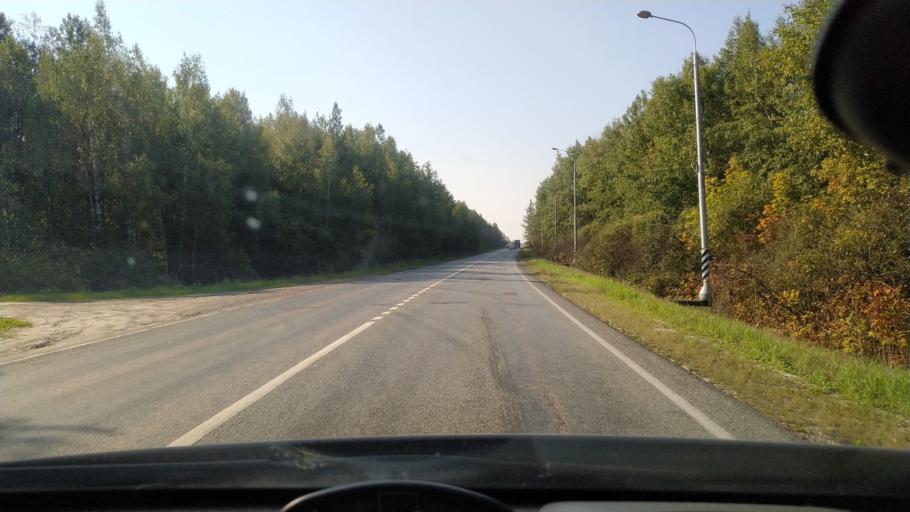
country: RU
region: Moskovskaya
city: Tugolesskiy Bor
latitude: 55.5304
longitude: 39.7101
